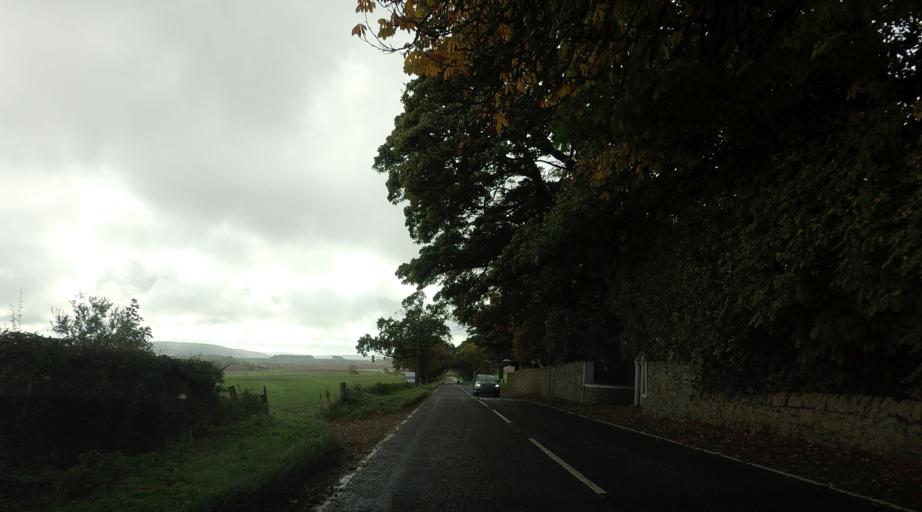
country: GB
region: Scotland
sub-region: Fife
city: Balmullo
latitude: 56.3745
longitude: -2.9284
